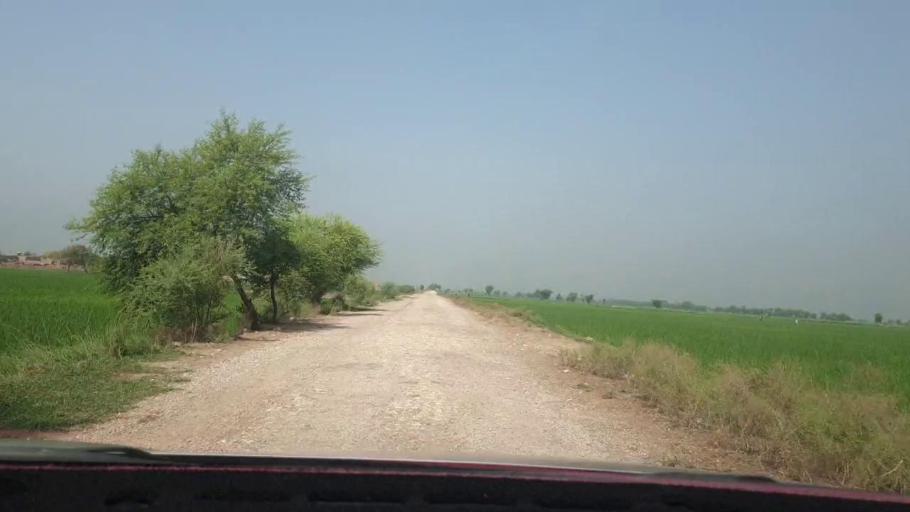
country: PK
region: Sindh
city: Nasirabad
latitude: 27.4298
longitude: 67.8737
